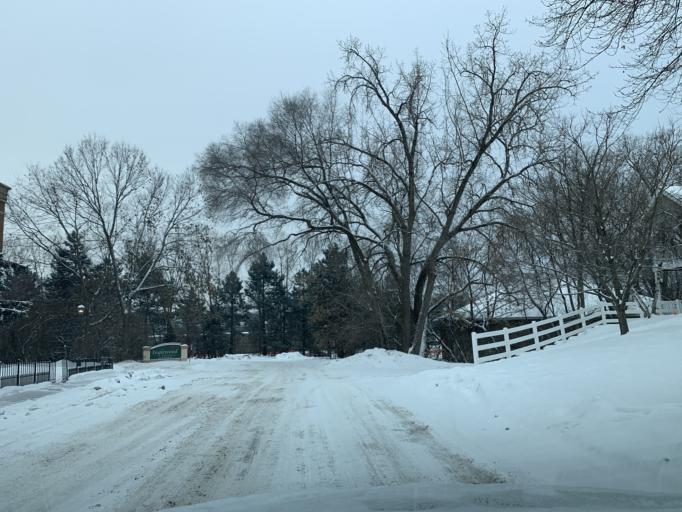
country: US
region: Minnesota
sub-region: Hennepin County
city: Saint Louis Park
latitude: 44.9464
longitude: -93.3327
